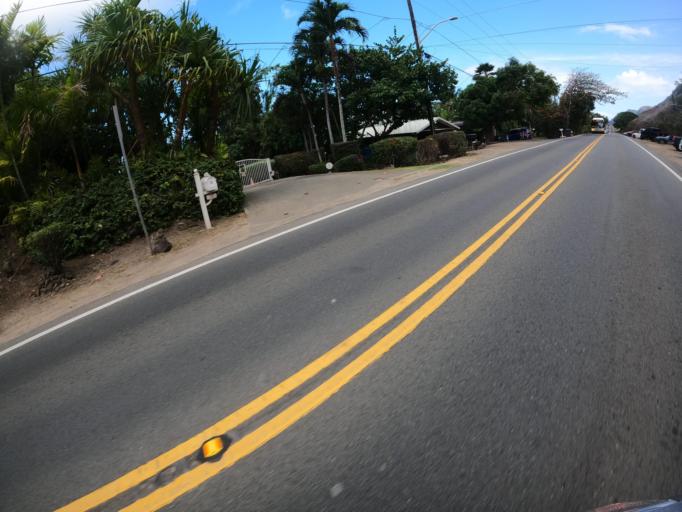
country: US
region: Hawaii
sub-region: Honolulu County
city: Waimanalo Beach
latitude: 21.3238
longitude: -157.6790
